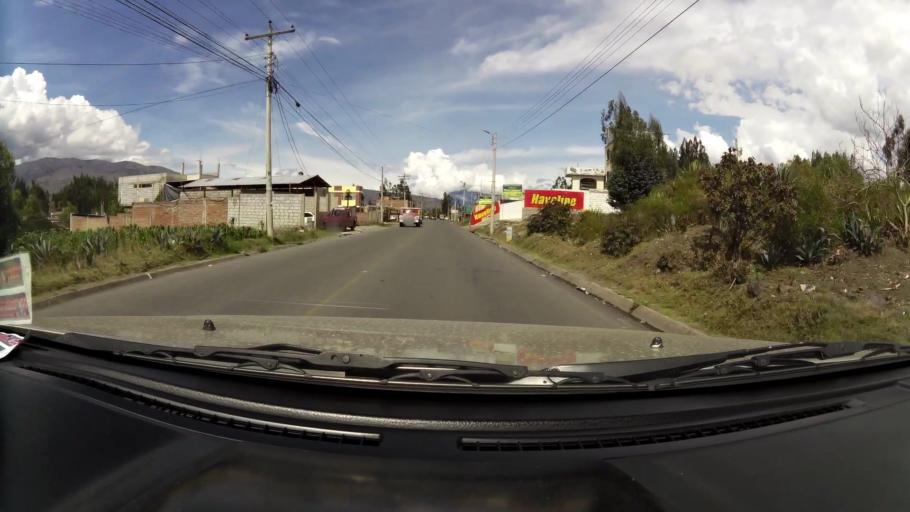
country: EC
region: Chimborazo
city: Riobamba
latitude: -1.6516
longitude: -78.6245
